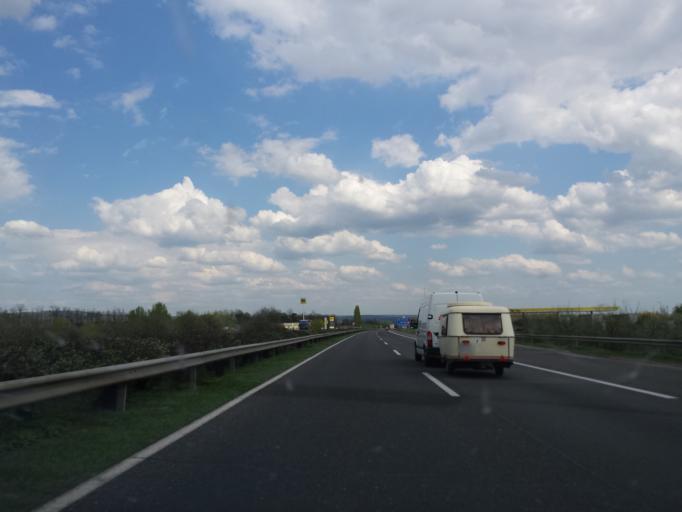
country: HU
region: Pest
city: Zsambek
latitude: 47.5110
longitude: 18.7326
